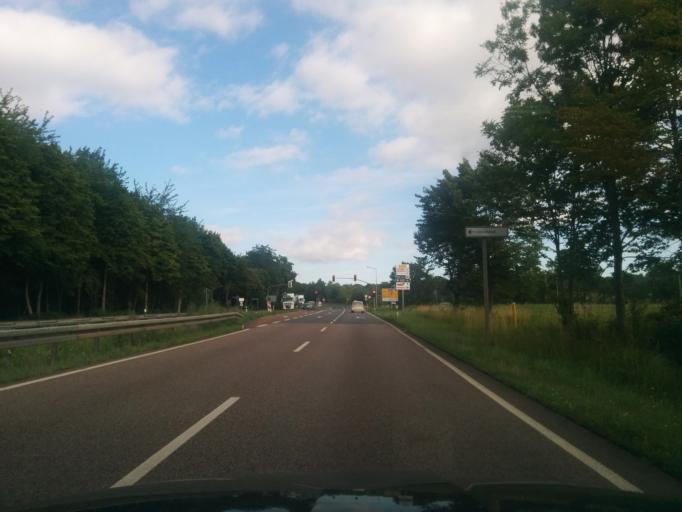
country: DE
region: Saxony-Anhalt
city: Zscherben
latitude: 51.4787
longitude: 11.8862
